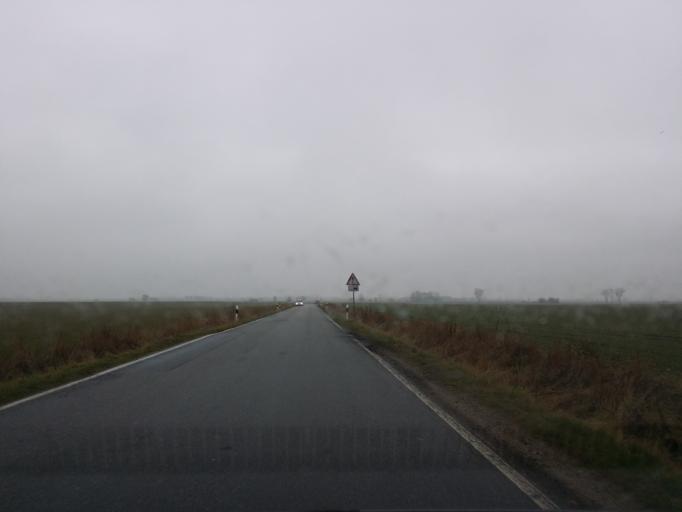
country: DE
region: Schleswig-Holstein
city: Fehmarn
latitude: 54.4340
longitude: 11.1874
